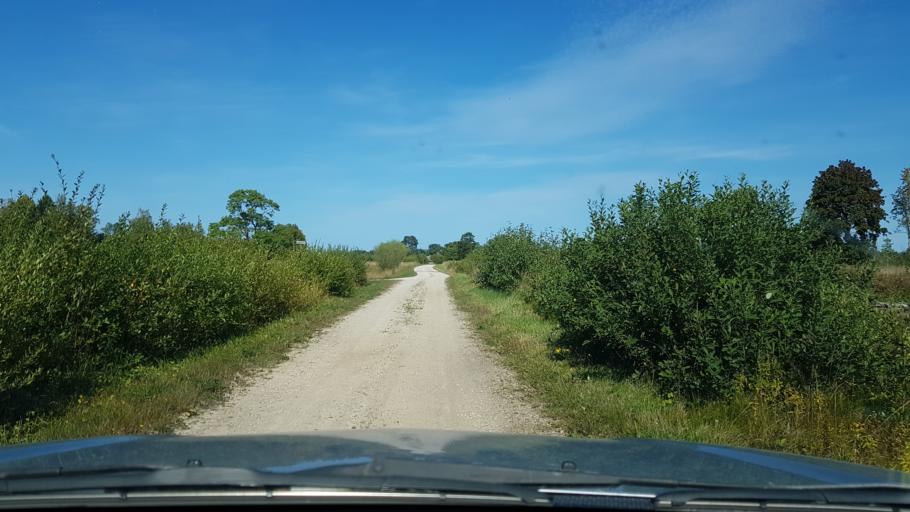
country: EE
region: Ida-Virumaa
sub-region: Sillamaee linn
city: Sillamae
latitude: 59.3803
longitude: 27.8108
